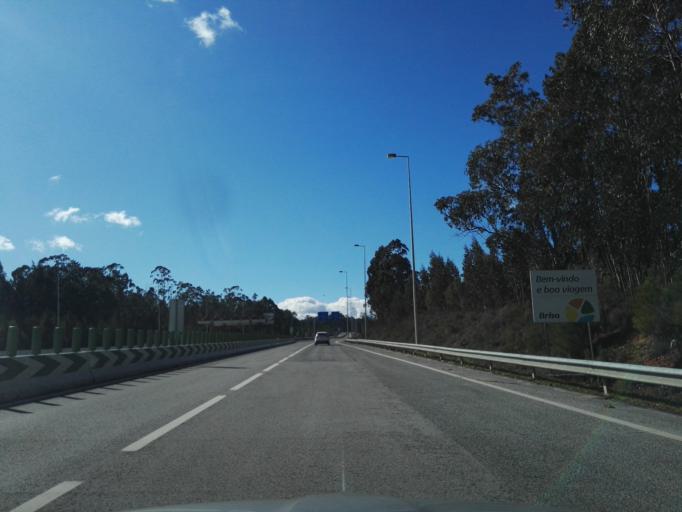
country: PT
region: Santarem
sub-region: Ourem
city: Fatima
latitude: 39.6272
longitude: -8.6888
